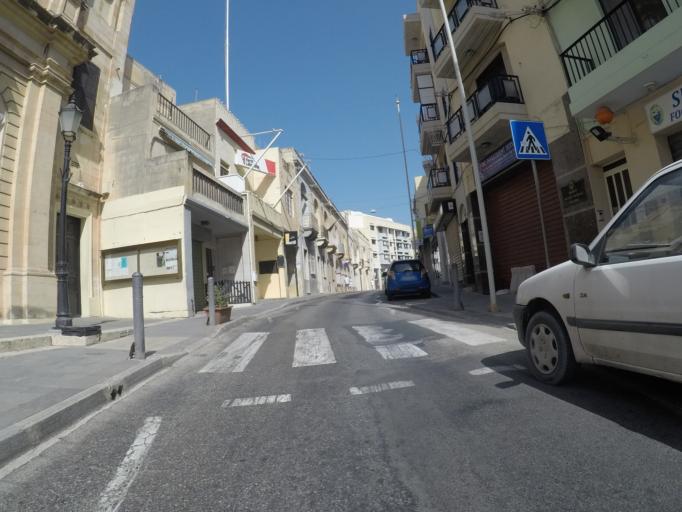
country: MT
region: Saint Paul's Bay
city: San Pawl il-Bahar
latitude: 35.9488
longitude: 14.4026
